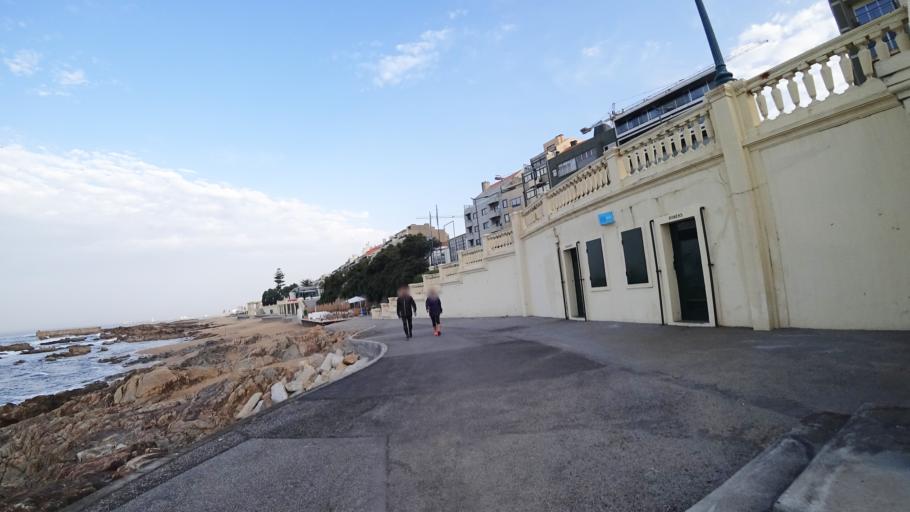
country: PT
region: Porto
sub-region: Matosinhos
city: Matosinhos
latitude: 41.1556
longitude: -8.6812
